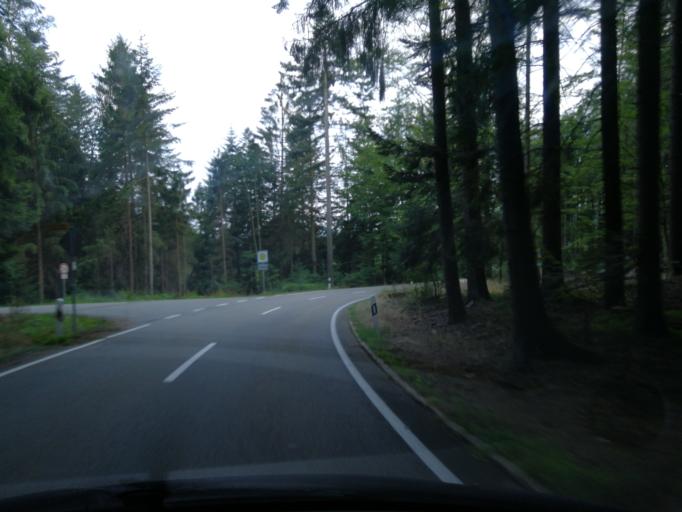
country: DE
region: Bavaria
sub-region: Lower Bavaria
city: Haibach
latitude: 49.0345
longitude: 12.7512
